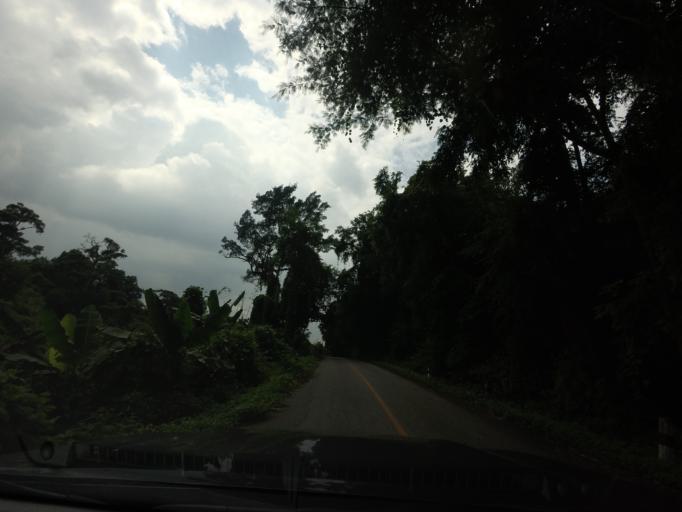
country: TH
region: Loei
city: Na Haeo
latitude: 17.7187
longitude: 100.9480
